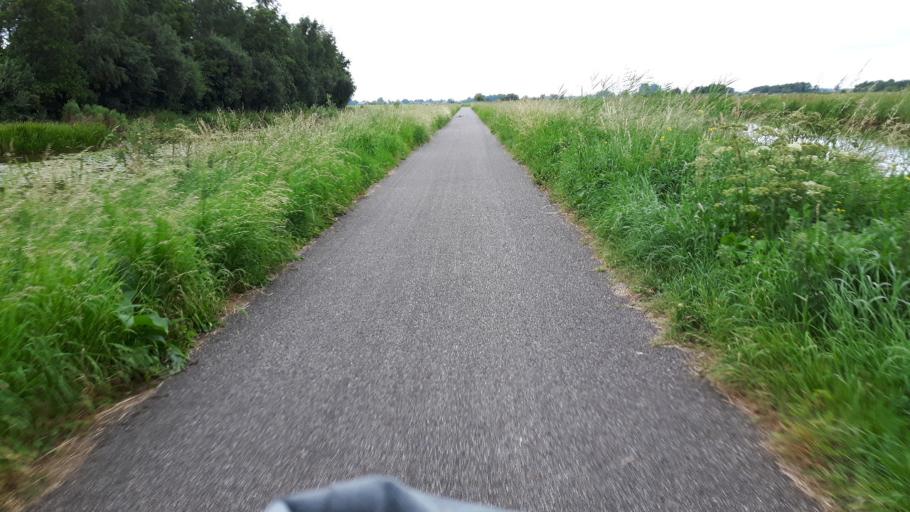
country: NL
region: South Holland
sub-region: Molenwaard
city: Nieuw-Lekkerland
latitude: 51.9389
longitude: 4.7378
